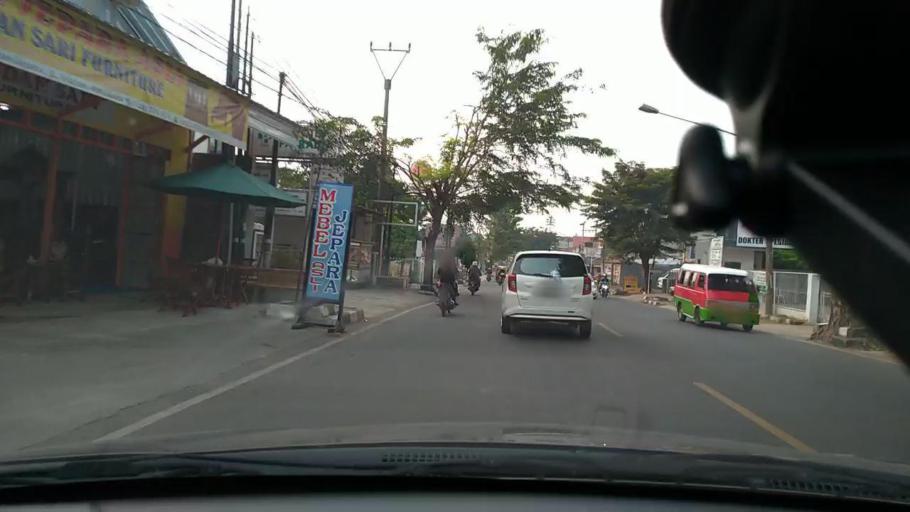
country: ID
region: West Java
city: Purwakarta
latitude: -6.5331
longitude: 107.4455
